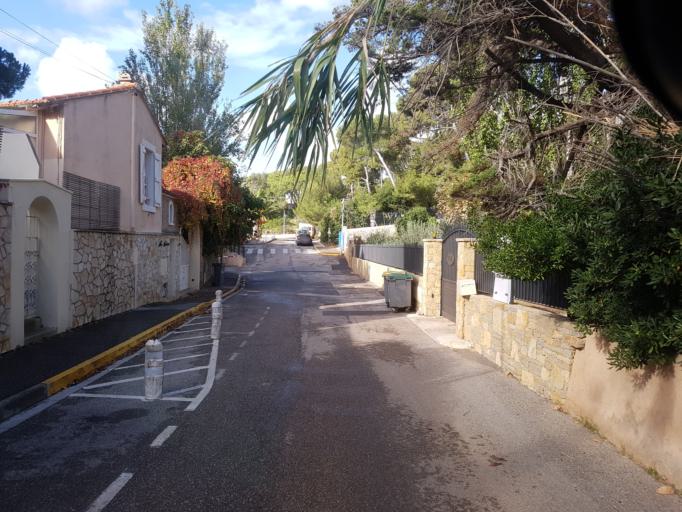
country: FR
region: Provence-Alpes-Cote d'Azur
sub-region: Departement du Var
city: Bandol
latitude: 43.1351
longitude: 5.7454
